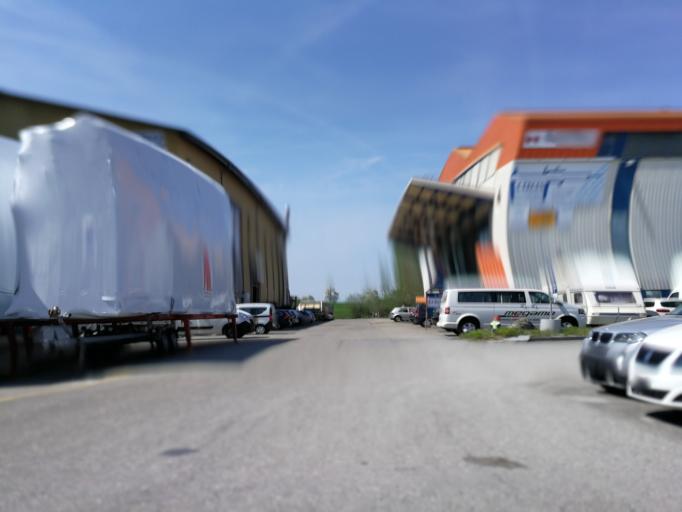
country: CH
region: Zurich
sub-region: Bezirk Hinwil
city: Hinwil
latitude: 47.3041
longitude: 8.8193
